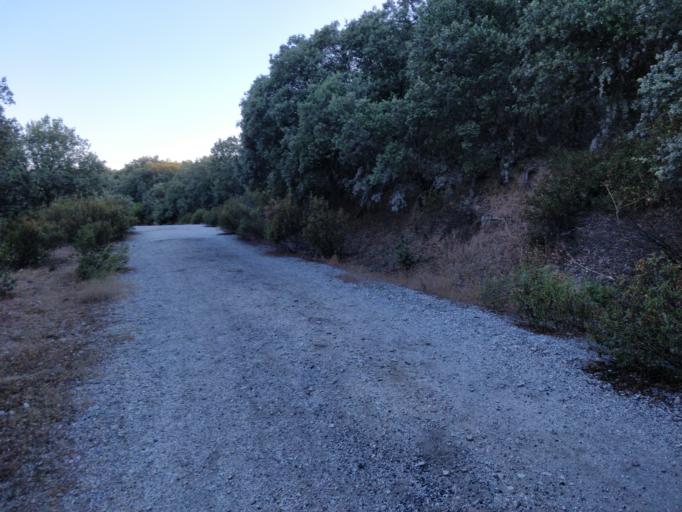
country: ES
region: Madrid
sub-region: Provincia de Madrid
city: Cervera de Buitrago
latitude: 40.9105
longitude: -3.5526
